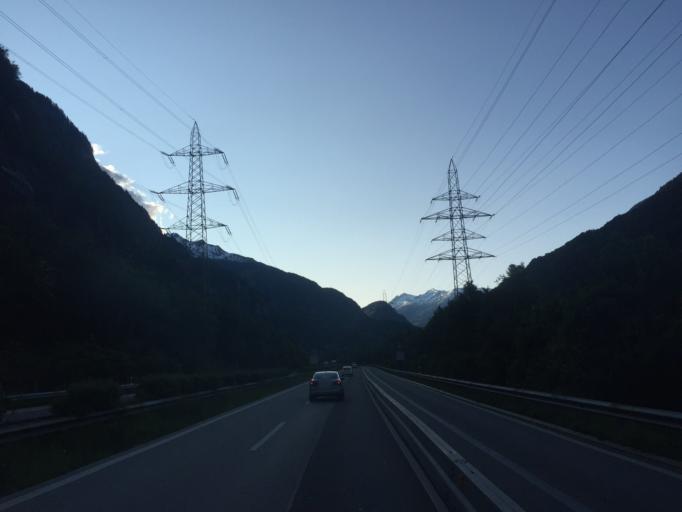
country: CH
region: Ticino
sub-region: Leventina District
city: Bodio
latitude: 46.3851
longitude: 8.8917
